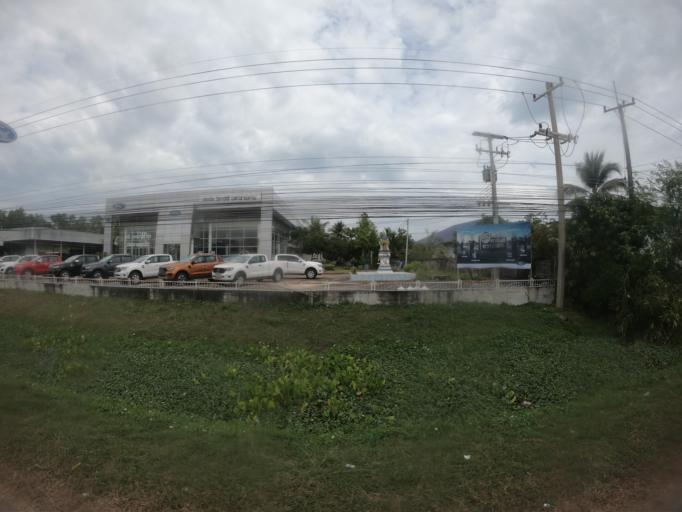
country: TH
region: Maha Sarakham
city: Maha Sarakham
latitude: 16.1659
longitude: 103.3319
